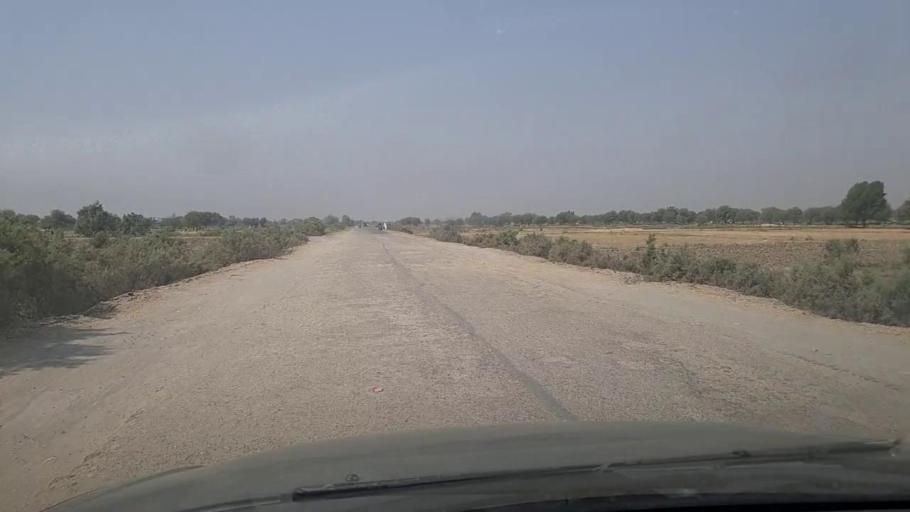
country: PK
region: Sindh
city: Khanpur
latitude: 27.9073
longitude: 69.5076
